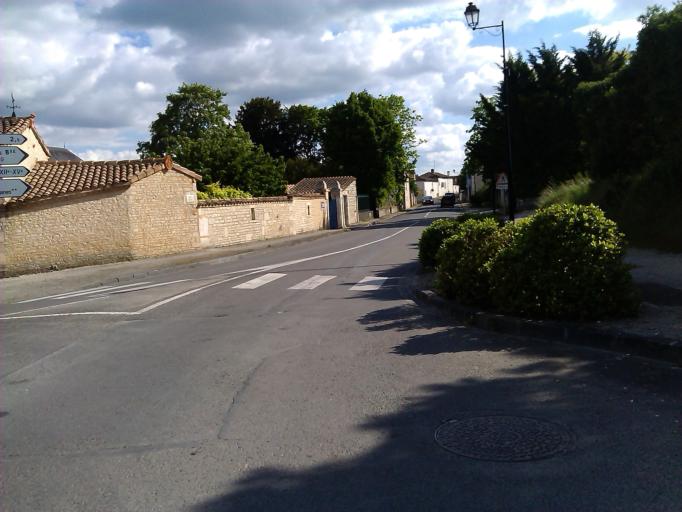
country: FR
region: Poitou-Charentes
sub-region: Departement de la Charente
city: Saint-Amant-de-Boixe
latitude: 45.8016
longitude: 0.1381
